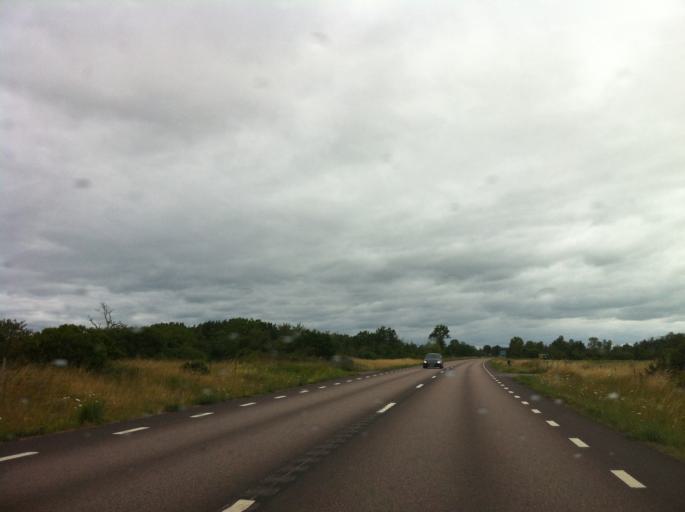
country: SE
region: Kalmar
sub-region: Borgholms Kommun
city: Borgholm
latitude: 57.0900
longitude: 16.9242
